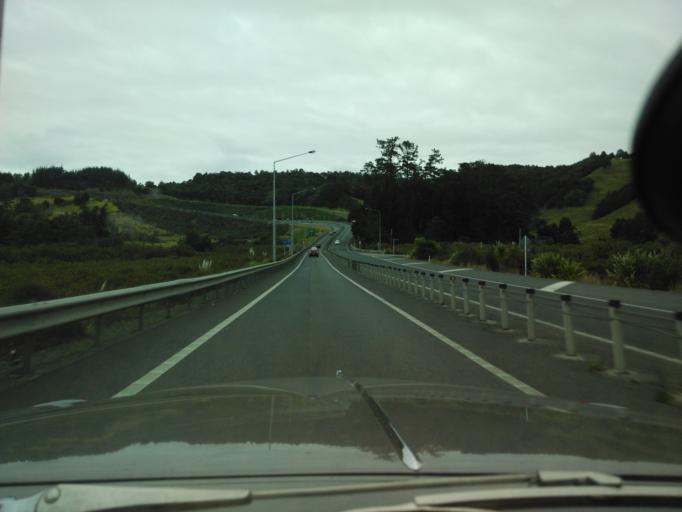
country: NZ
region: Auckland
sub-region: Auckland
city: Warkworth
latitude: -36.5264
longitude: 174.6777
